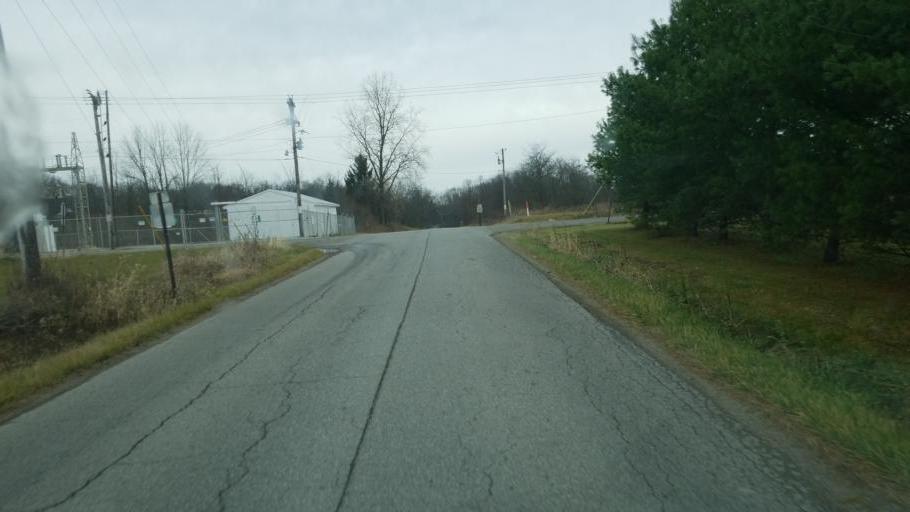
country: US
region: Ohio
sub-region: Delaware County
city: Ashley
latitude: 40.3612
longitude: -82.9264
